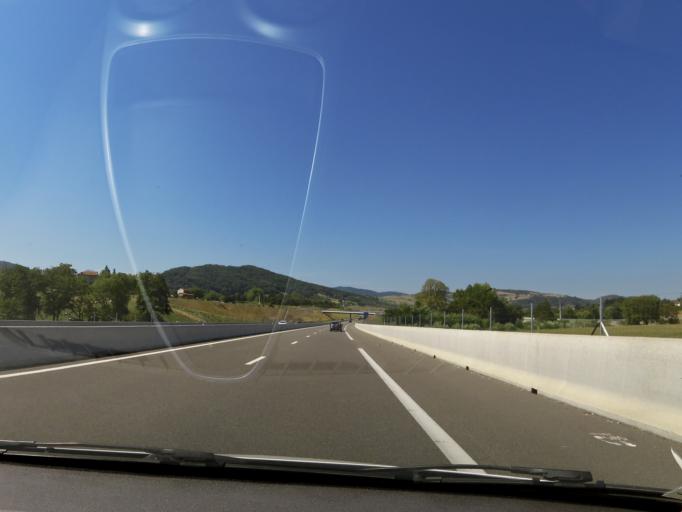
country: FR
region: Rhone-Alpes
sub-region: Departement du Rhone
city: Saint-Romain-de-Popey
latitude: 45.8747
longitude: 4.5230
